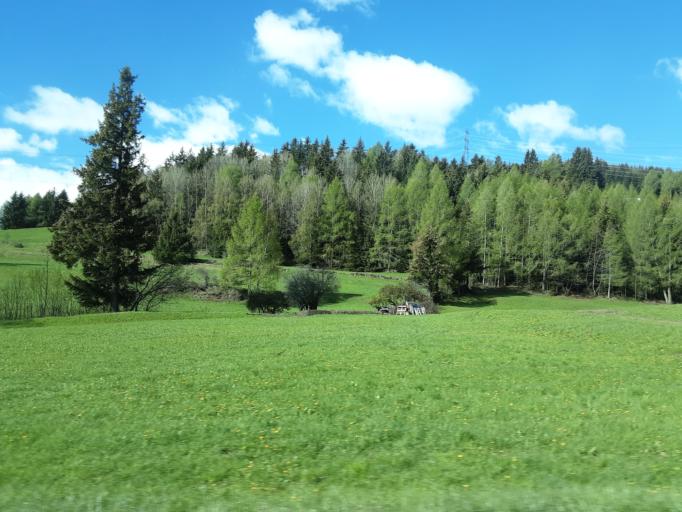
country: IT
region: Lombardy
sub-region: Provincia di Sondrio
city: Bormio
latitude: 46.4754
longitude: 10.3530
